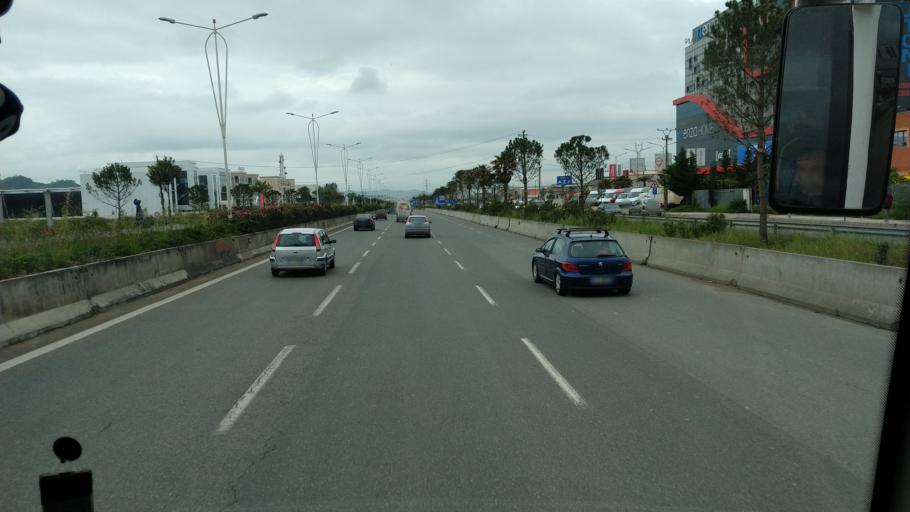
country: AL
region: Tirane
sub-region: Rrethi i Tiranes
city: Paskuqan
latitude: 41.3446
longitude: 19.7715
